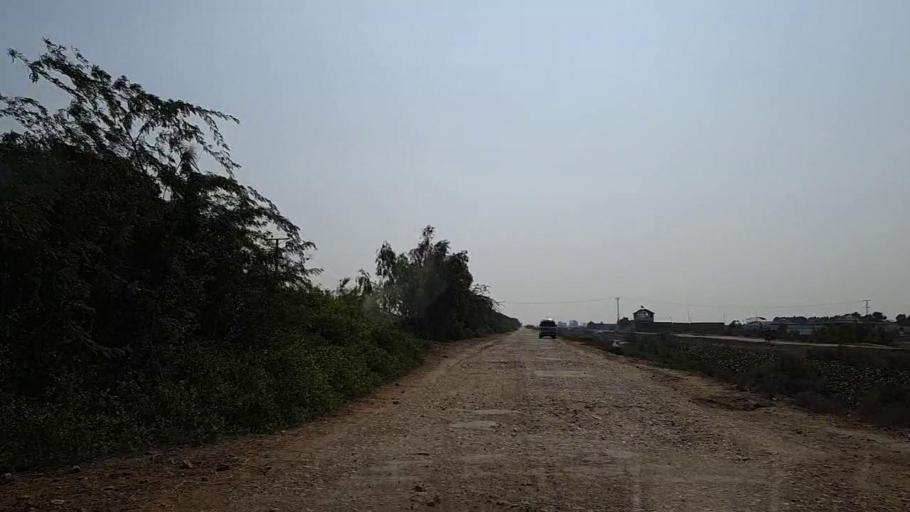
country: PK
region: Sindh
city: Thatta
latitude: 24.7222
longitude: 67.7684
